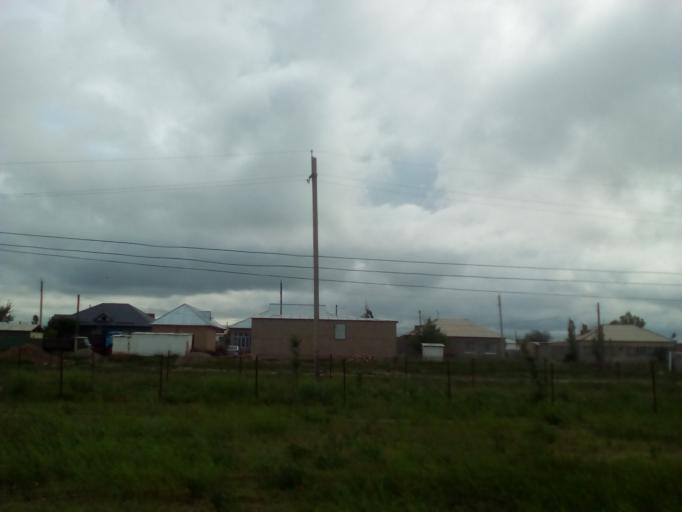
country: KZ
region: Ongtustik Qazaqstan
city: Sholaqqkorghan
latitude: 43.7535
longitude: 69.1933
